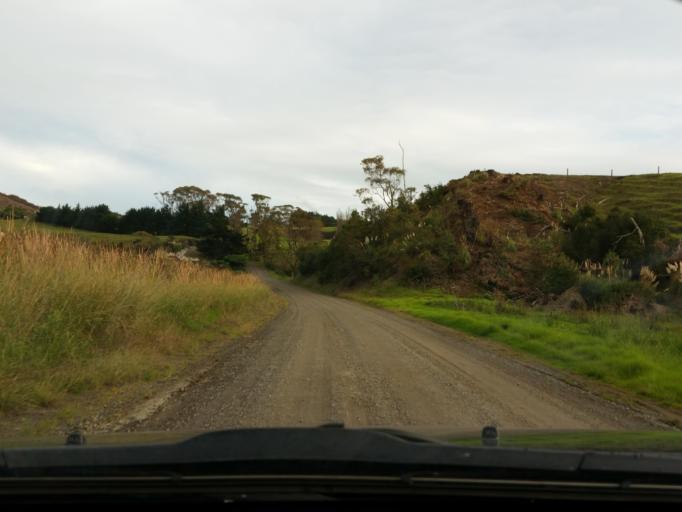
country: NZ
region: Northland
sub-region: Kaipara District
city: Dargaville
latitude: -35.8352
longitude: 173.6610
